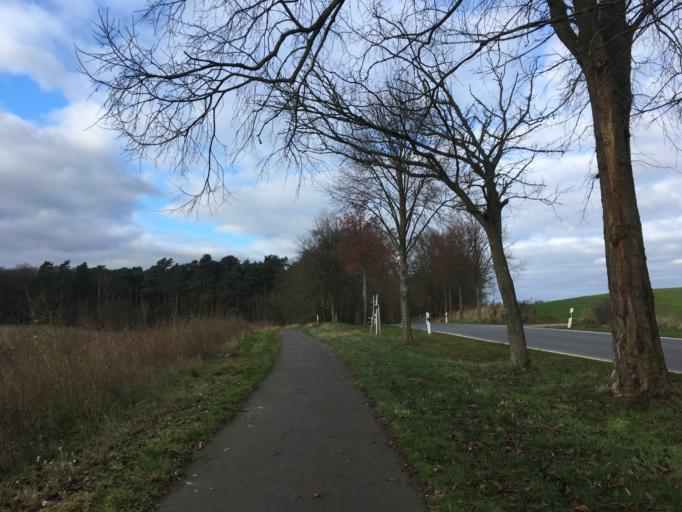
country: DE
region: Brandenburg
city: Muncheberg
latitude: 52.5504
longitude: 14.1526
